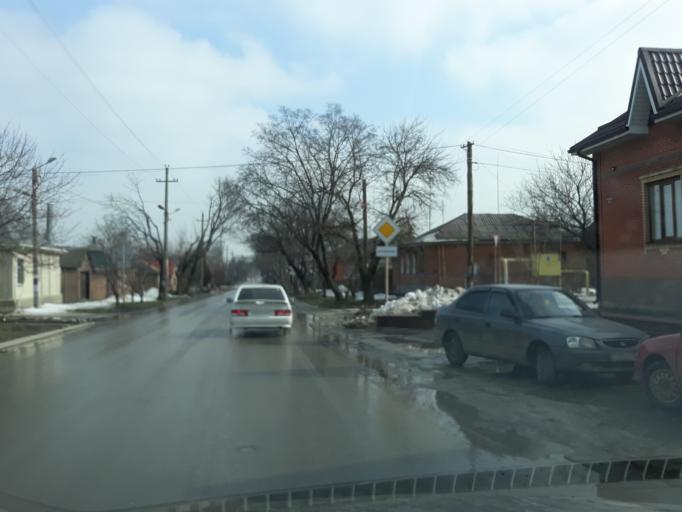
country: RU
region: Rostov
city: Taganrog
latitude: 47.2149
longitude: 38.9007
